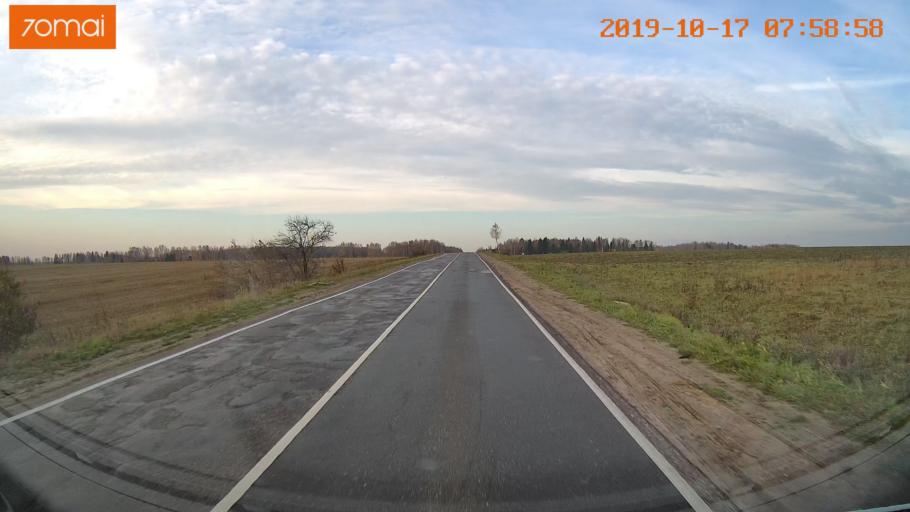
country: RU
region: Vladimir
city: Bavleny
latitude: 56.3978
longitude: 39.5476
